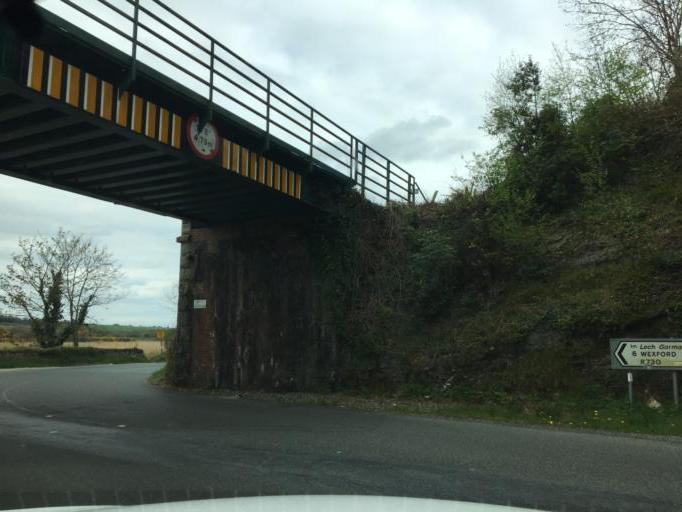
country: IE
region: Leinster
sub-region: Loch Garman
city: Loch Garman
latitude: 52.3523
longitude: -6.5373
